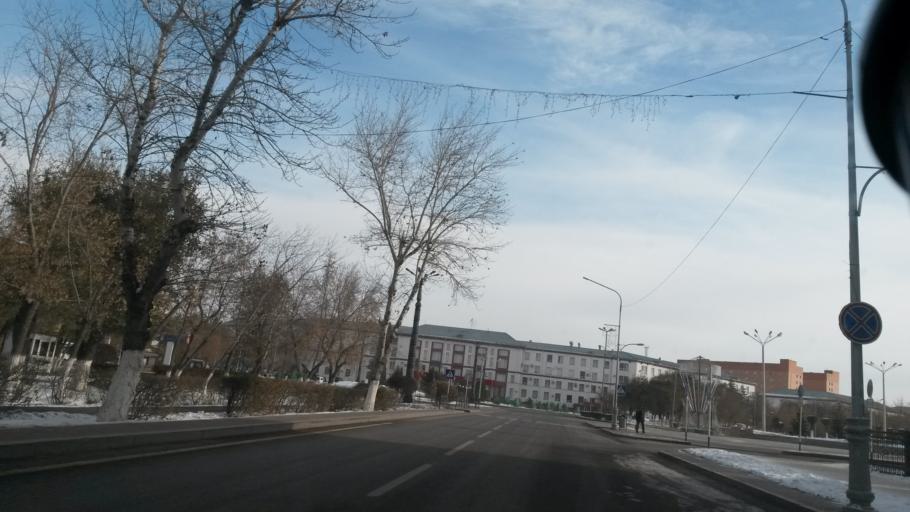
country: KZ
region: Qaraghandy
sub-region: Qaraghandy Qalasy
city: Karagandy
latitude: 49.8173
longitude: 73.1014
